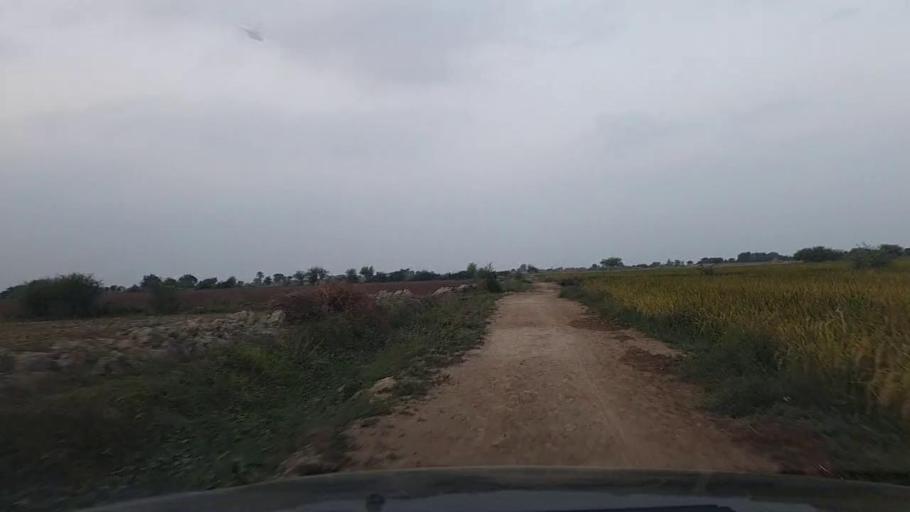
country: PK
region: Sindh
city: Jati
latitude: 24.5074
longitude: 68.3931
